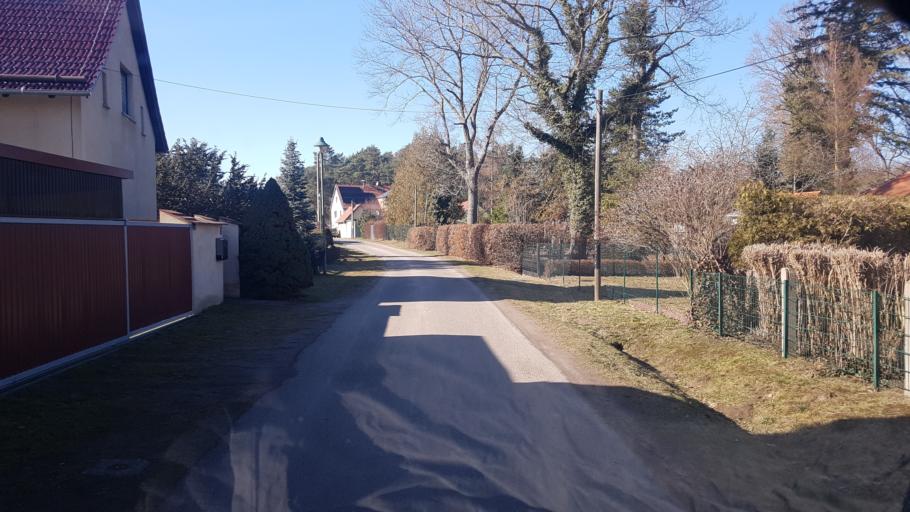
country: DE
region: Brandenburg
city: Lebusa
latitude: 51.8132
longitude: 13.3976
